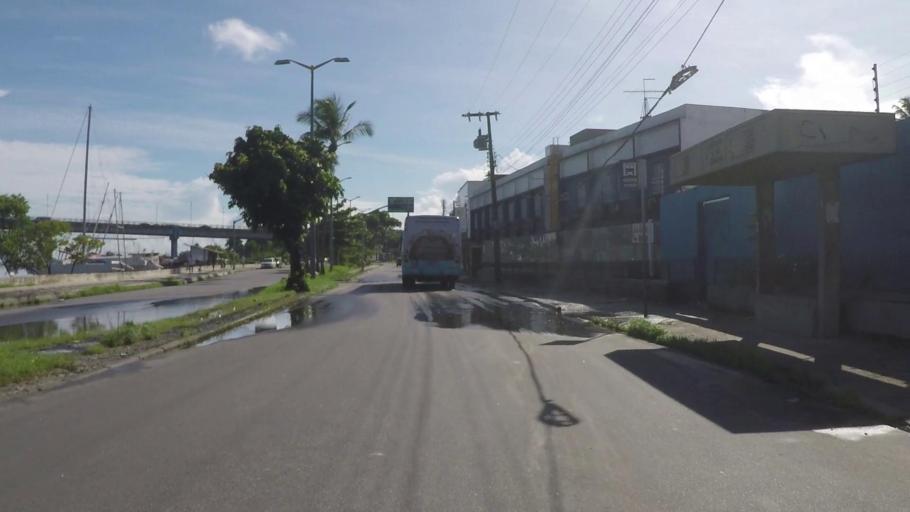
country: BR
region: Ceara
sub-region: Fortaleza
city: Fortaleza
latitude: -3.7019
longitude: -38.5898
